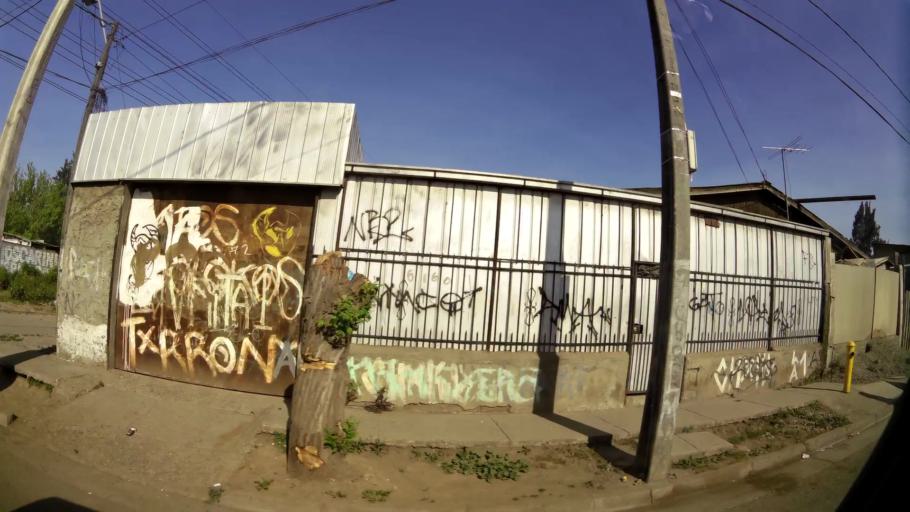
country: CL
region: Santiago Metropolitan
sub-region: Provincia de Santiago
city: Lo Prado
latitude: -33.4242
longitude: -70.7544
